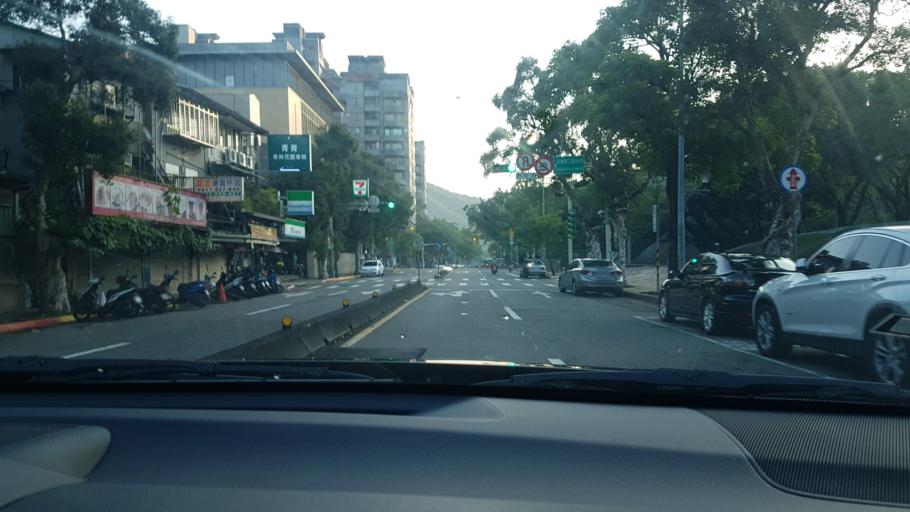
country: TW
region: Taipei
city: Taipei
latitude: 25.1009
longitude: 121.5513
